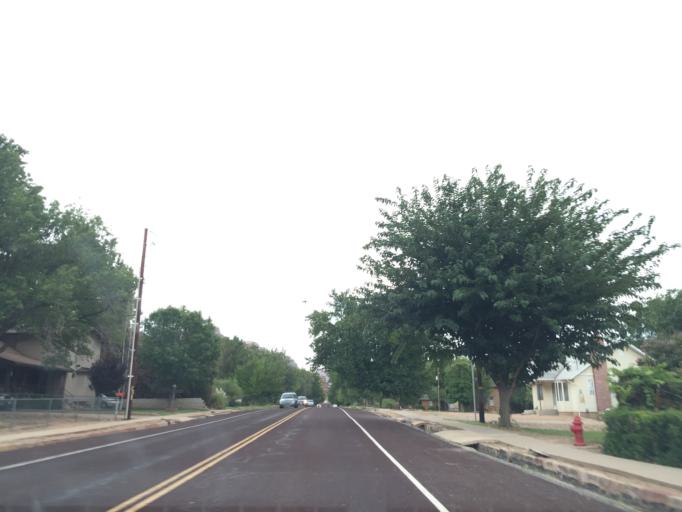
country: US
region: Utah
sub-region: Washington County
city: Hildale
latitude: 37.1610
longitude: -113.0472
